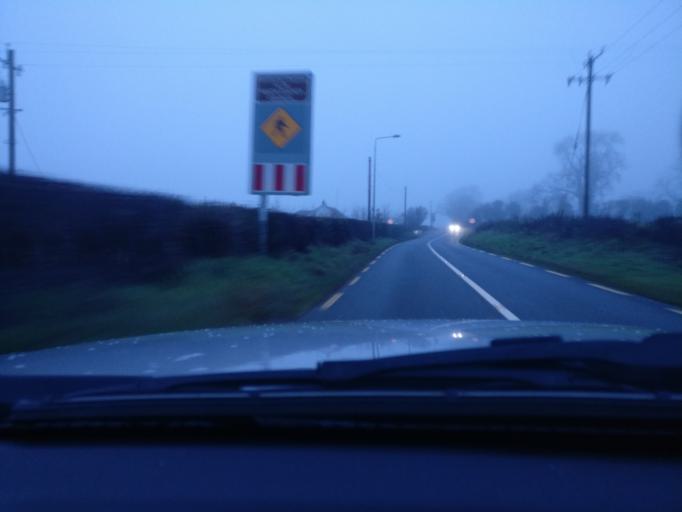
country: IE
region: Leinster
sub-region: An Mhi
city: Athboy
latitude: 53.6275
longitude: -6.9060
